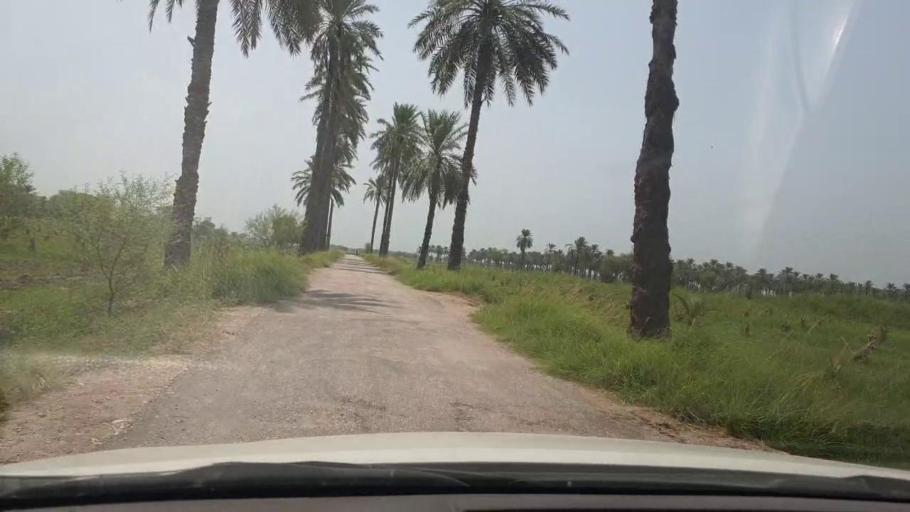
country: PK
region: Sindh
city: Shikarpur
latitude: 28.0202
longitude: 68.6169
